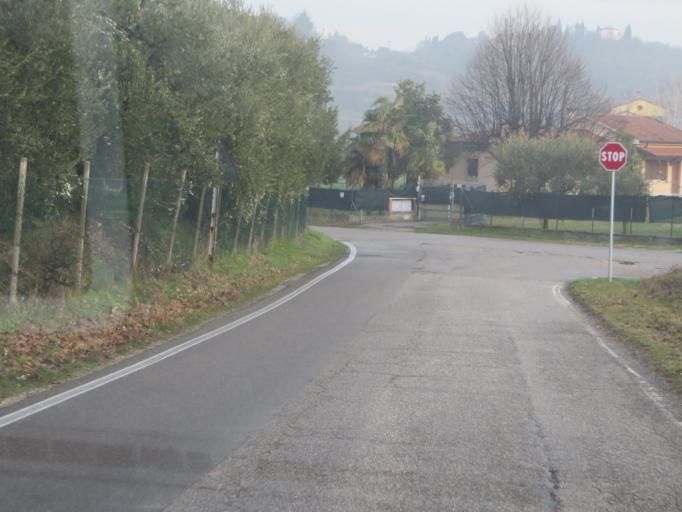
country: IT
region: Veneto
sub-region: Provincia di Verona
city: Pastrengo
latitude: 45.4797
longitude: 10.8083
